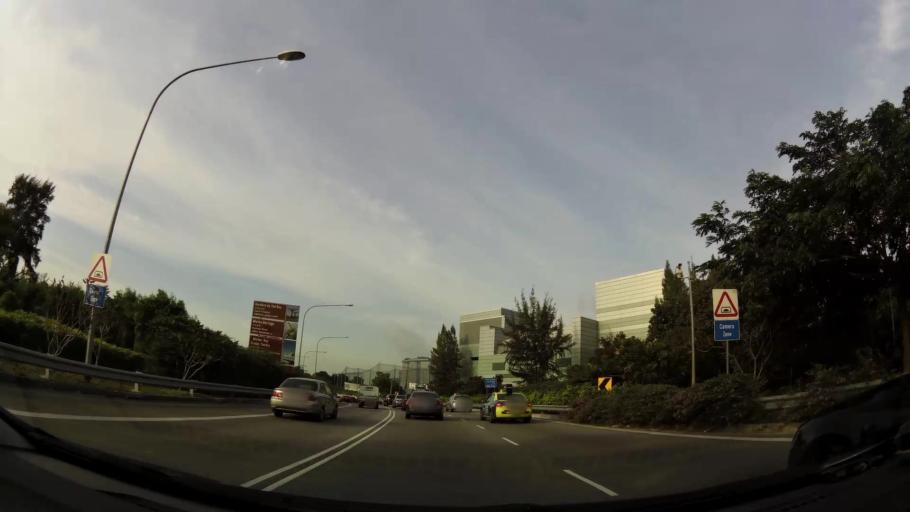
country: SG
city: Singapore
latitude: 1.2949
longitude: 103.8769
